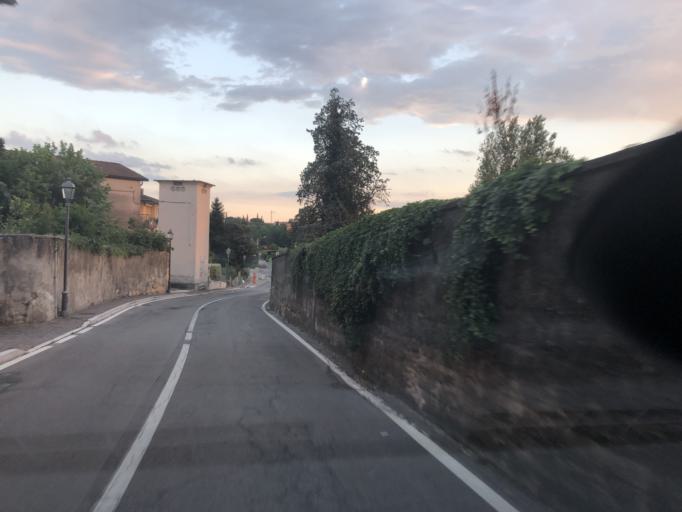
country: IT
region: Veneto
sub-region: Provincia di Verona
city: Settimo
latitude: 45.4755
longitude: 10.9043
